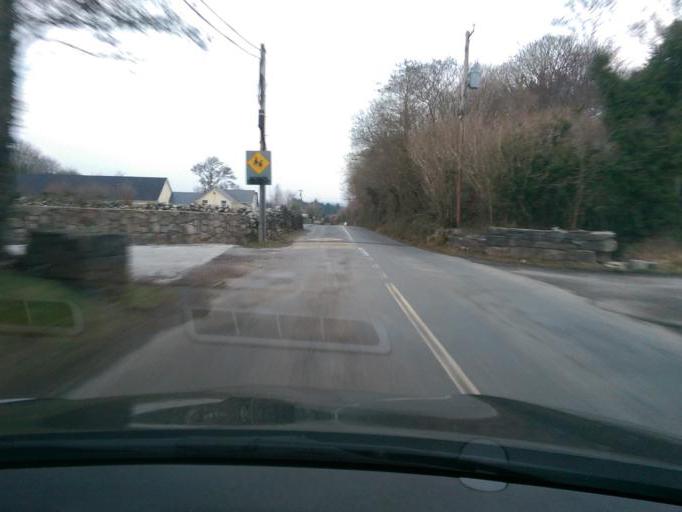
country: IE
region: Connaught
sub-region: County Galway
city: Moycullen
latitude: 53.3058
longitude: -9.1538
